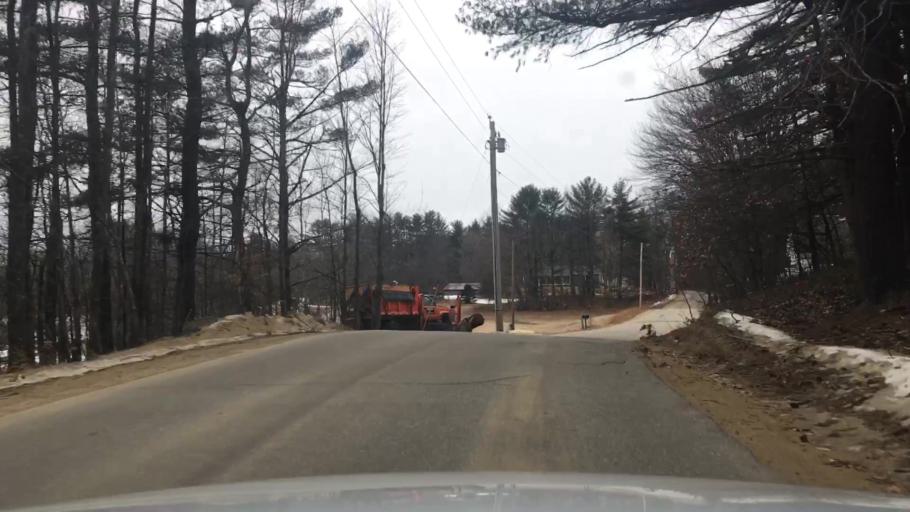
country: US
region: New Hampshire
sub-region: Strafford County
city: Rochester
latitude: 43.3432
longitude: -70.9571
